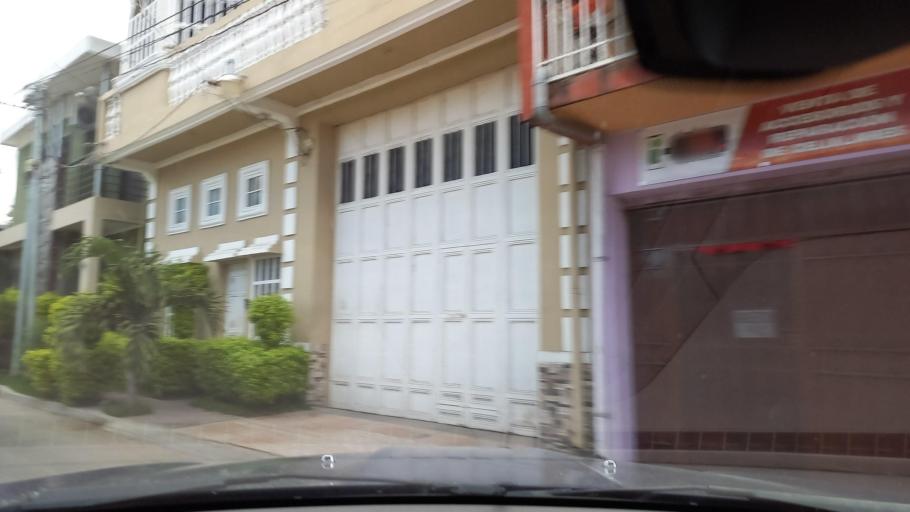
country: SV
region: Santa Ana
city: Metapan
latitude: 14.3291
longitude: -89.4417
